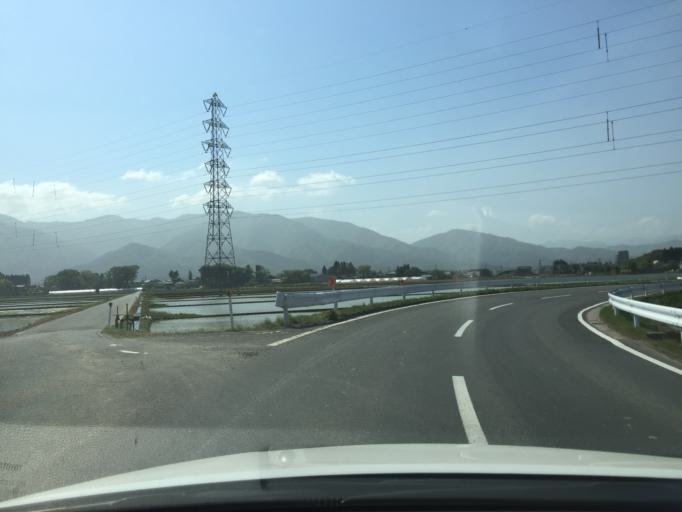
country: JP
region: Niigata
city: Gosen
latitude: 37.7363
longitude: 139.2086
